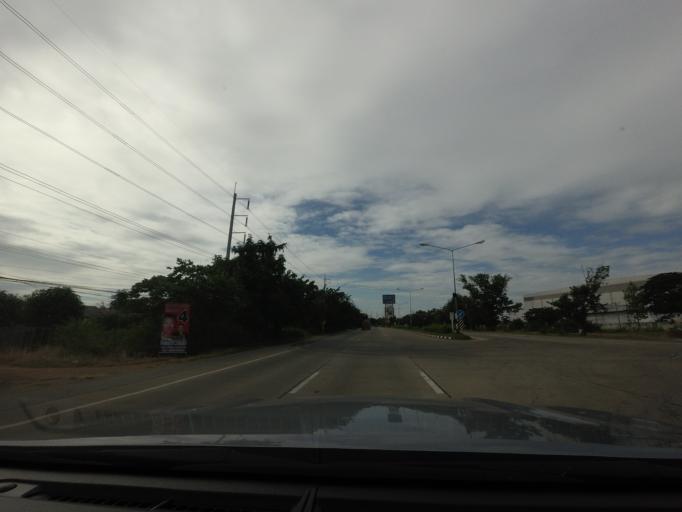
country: TH
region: Suphan Buri
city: Doem Bang Nang Buat
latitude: 14.9050
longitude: 100.0870
